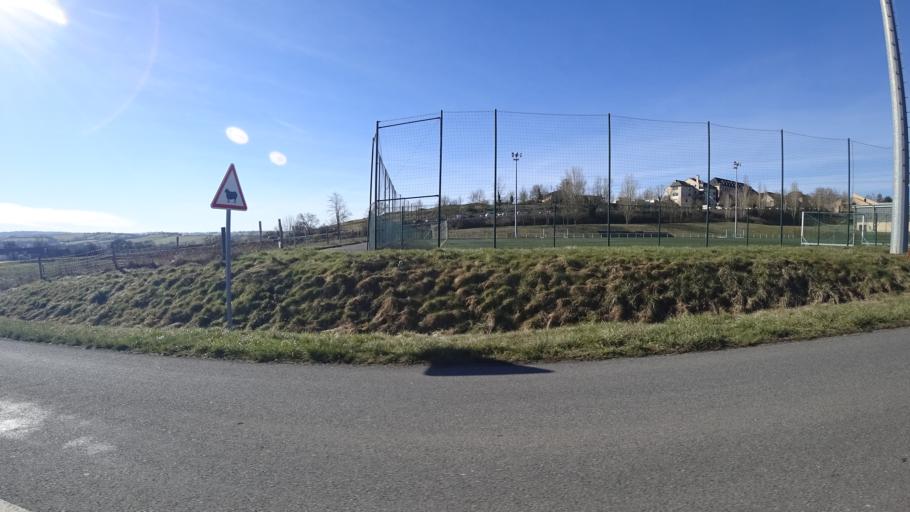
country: FR
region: Midi-Pyrenees
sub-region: Departement de l'Aveyron
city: Sebazac-Concoures
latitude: 44.3834
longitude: 2.5890
